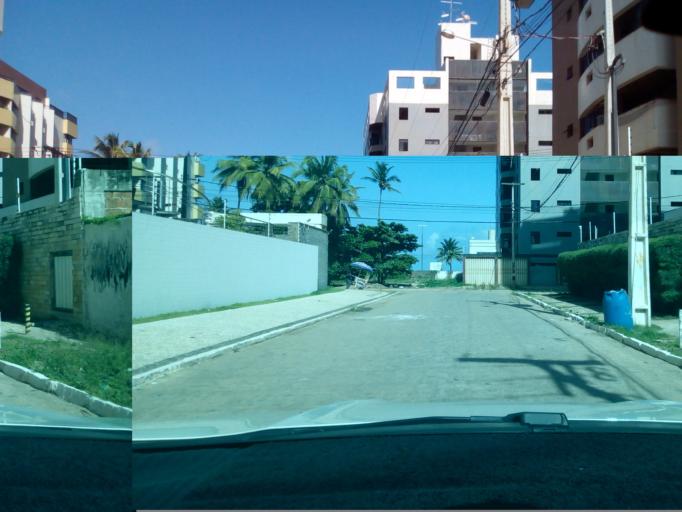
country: BR
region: Paraiba
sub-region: Cabedelo
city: Cabedelo
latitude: -7.0435
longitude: -34.8423
